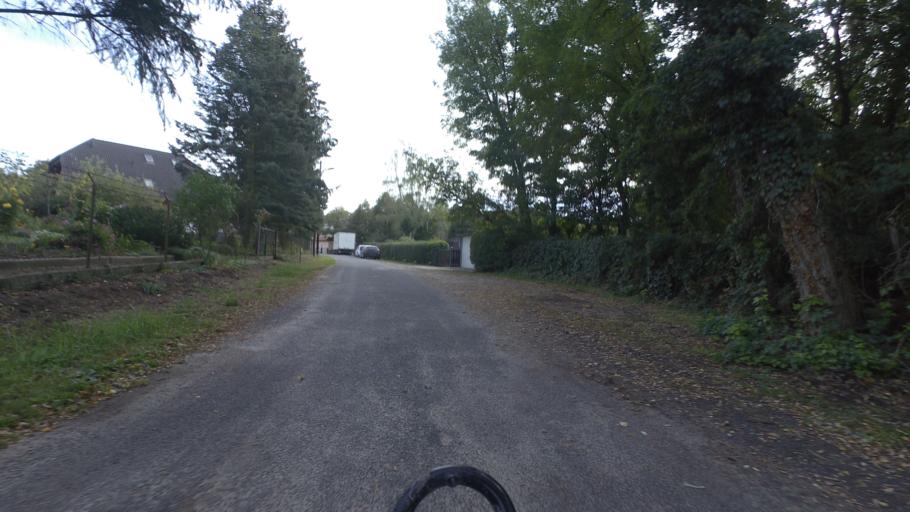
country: DE
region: Brandenburg
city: Ludwigsfelde
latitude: 52.3076
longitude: 13.2390
